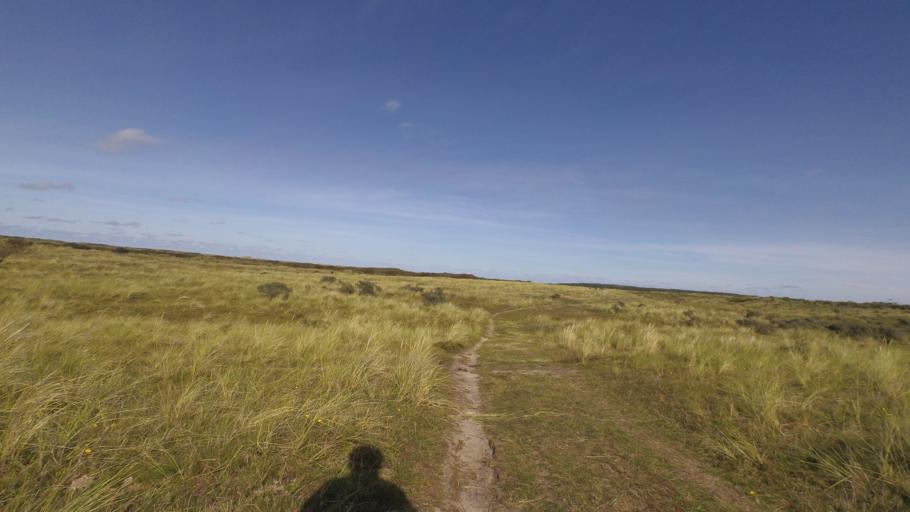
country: NL
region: Friesland
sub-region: Gemeente Ameland
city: Nes
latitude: 53.4489
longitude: 5.7337
